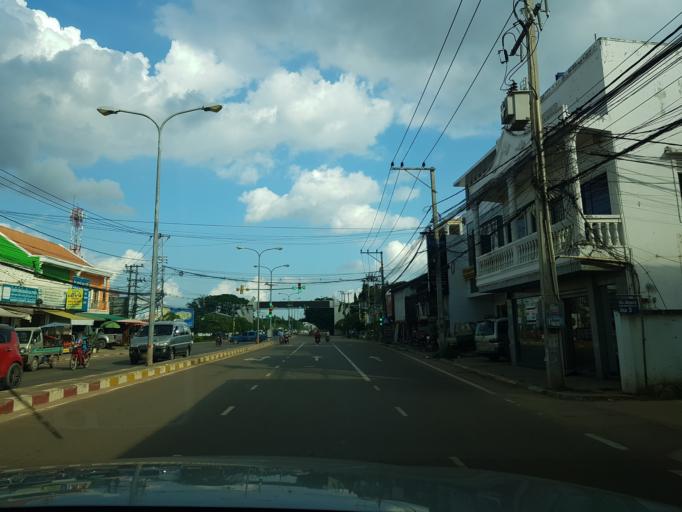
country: TH
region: Nong Khai
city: Si Chiang Mai
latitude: 17.9721
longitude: 102.5658
